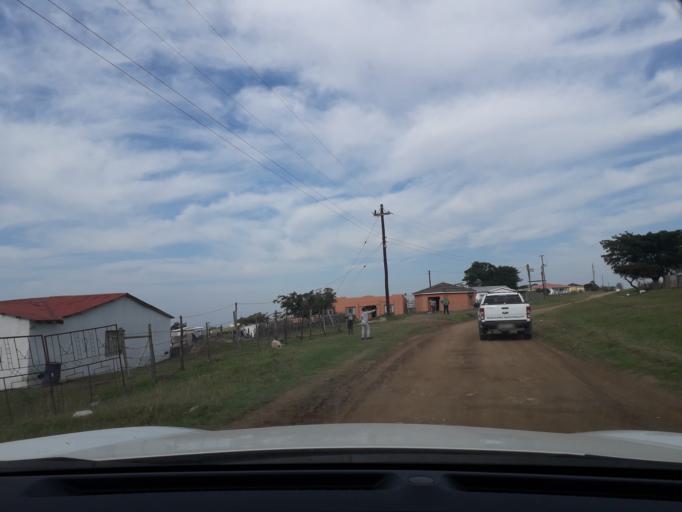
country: ZA
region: Eastern Cape
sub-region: Buffalo City Metropolitan Municipality
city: Bhisho
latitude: -32.9864
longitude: 27.3610
